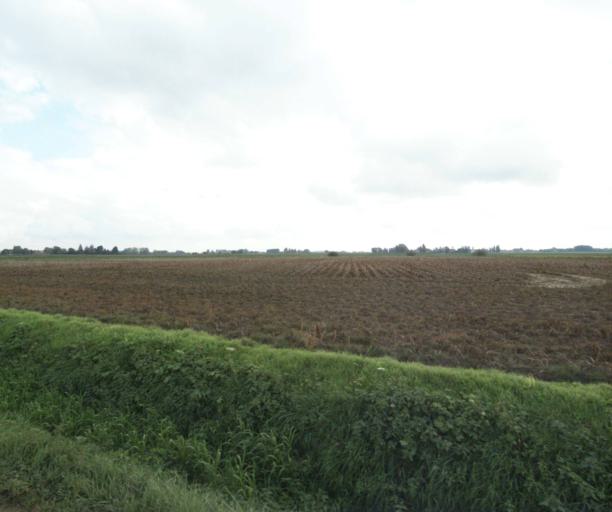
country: FR
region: Nord-Pas-de-Calais
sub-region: Departement du Nord
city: Herlies
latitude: 50.5953
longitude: 2.8613
